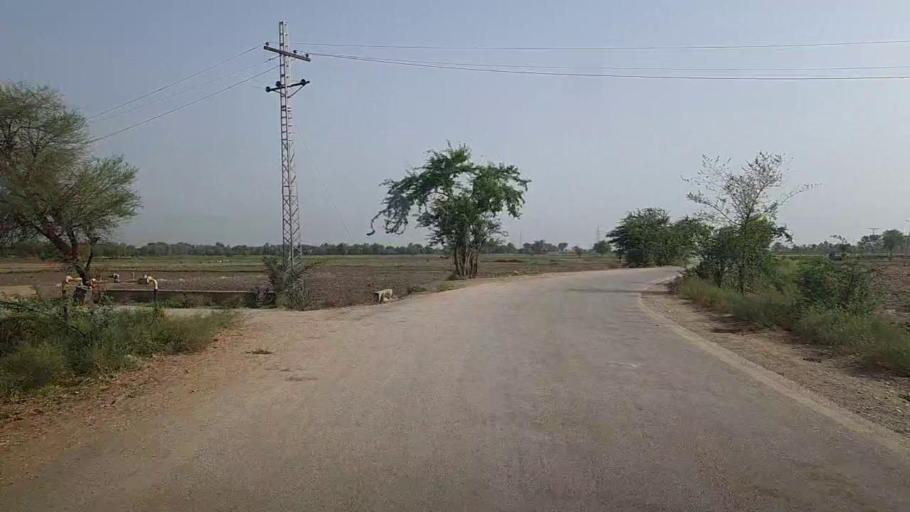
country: PK
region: Sindh
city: Khairpur Nathan Shah
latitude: 27.1043
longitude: 67.7571
